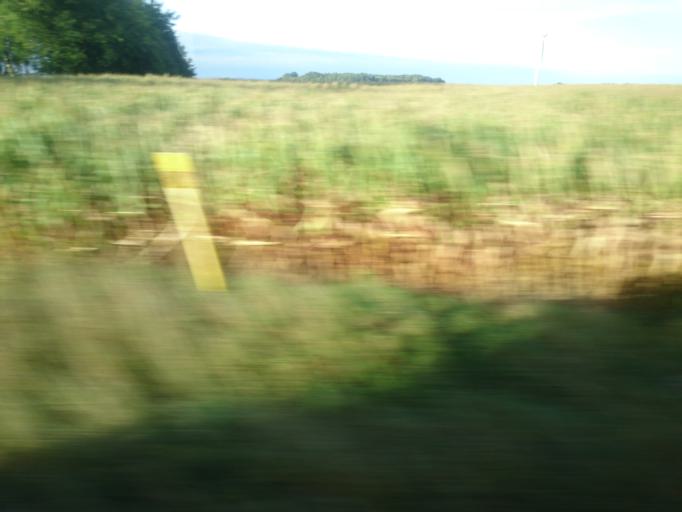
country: DE
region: Mecklenburg-Vorpommern
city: Anklam
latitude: 53.9085
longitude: 13.6565
